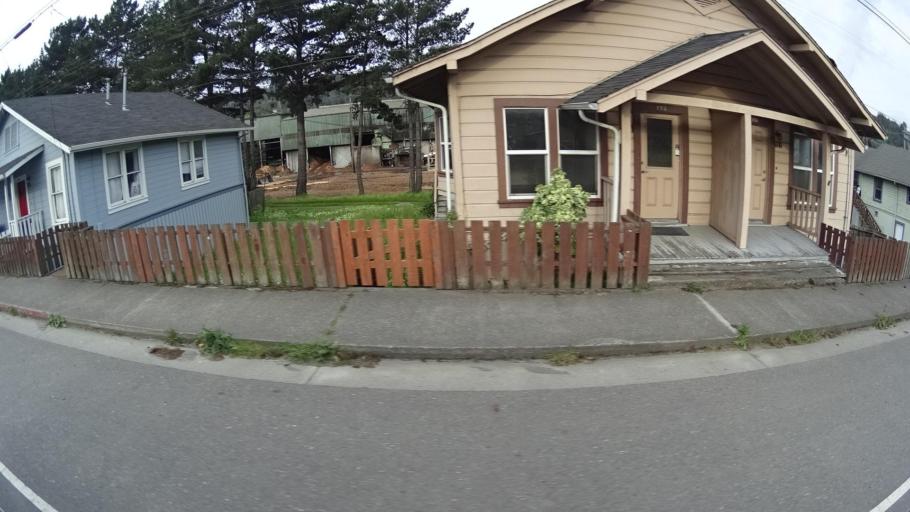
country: US
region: California
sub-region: Humboldt County
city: Rio Dell
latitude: 40.4803
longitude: -124.1030
